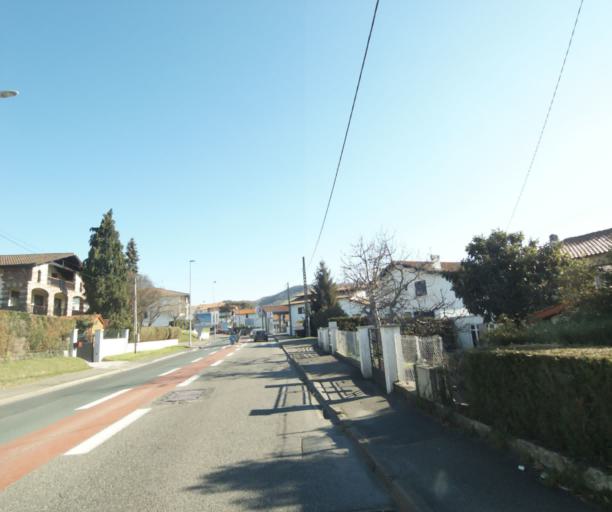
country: ES
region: Basque Country
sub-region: Provincia de Guipuzcoa
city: Irun
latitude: 43.3478
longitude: -1.7668
